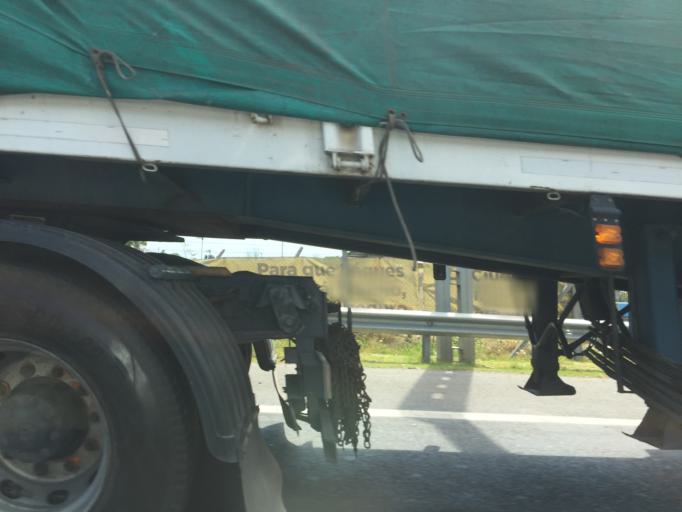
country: AR
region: Buenos Aires F.D.
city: Retiro
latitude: -34.5683
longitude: -58.4059
